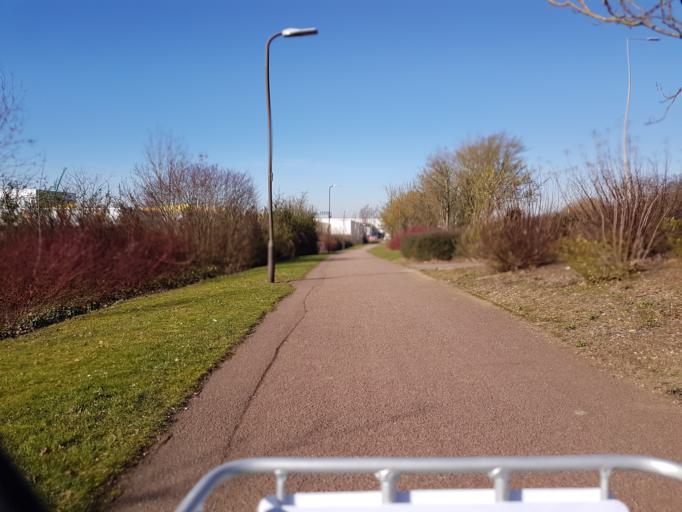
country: GB
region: England
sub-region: Milton Keynes
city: Milton Keynes
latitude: 52.0262
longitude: -0.7598
